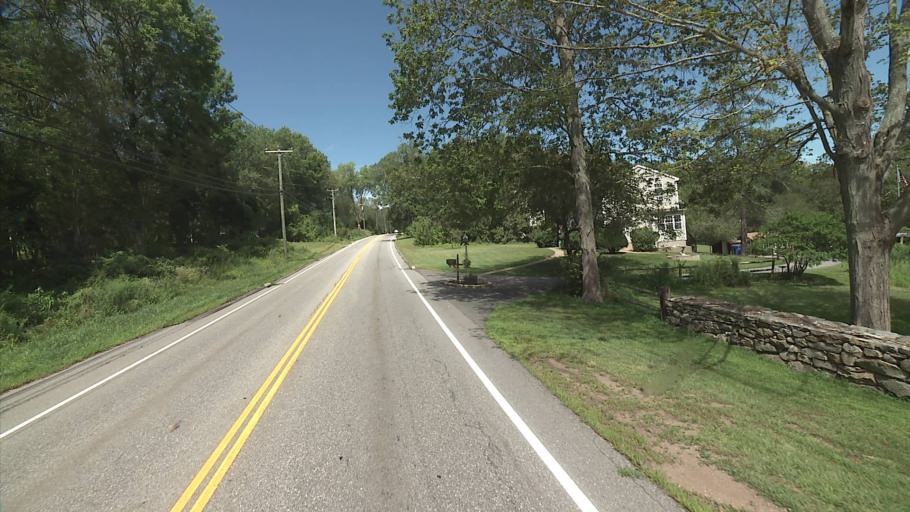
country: US
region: Connecticut
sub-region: Tolland County
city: Mansfield City
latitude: 41.7555
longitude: -72.1938
